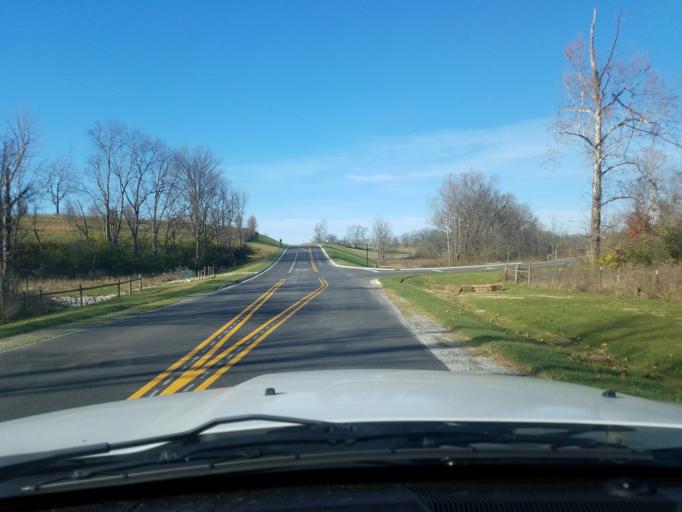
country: US
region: Indiana
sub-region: Clark County
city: Oak Park
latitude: 38.3629
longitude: -85.6793
